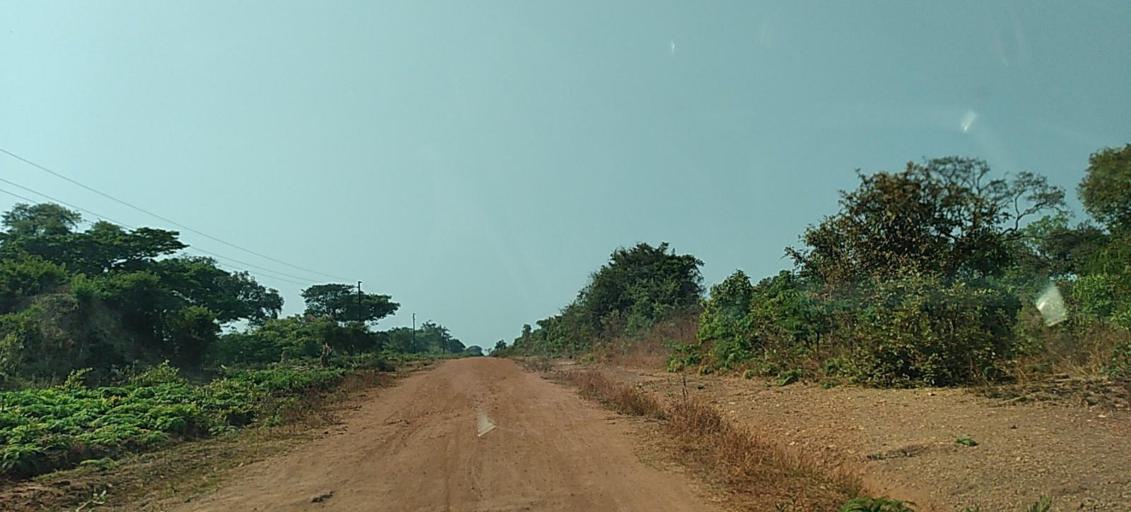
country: ZM
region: Copperbelt
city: Chingola
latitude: -12.9105
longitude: 27.3721
